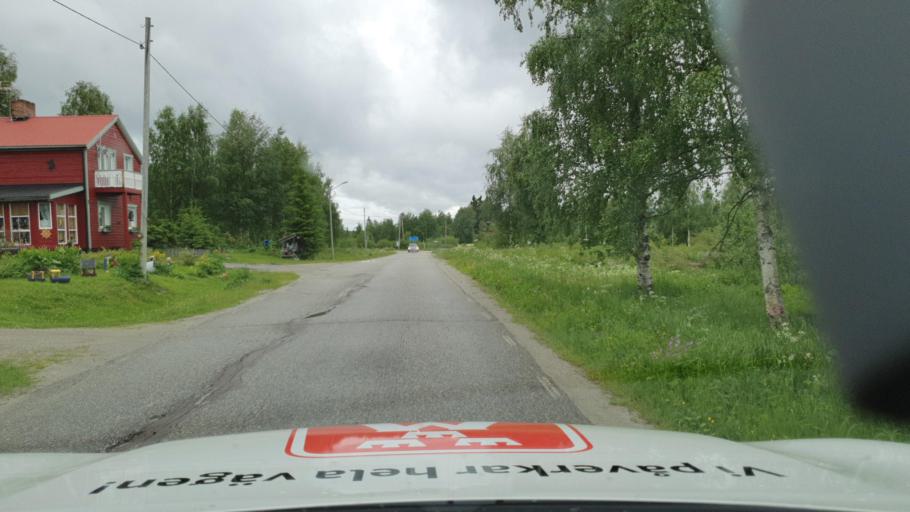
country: SE
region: Vaesterbotten
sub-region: Dorotea Kommun
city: Dorotea
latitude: 64.1026
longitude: 16.6424
